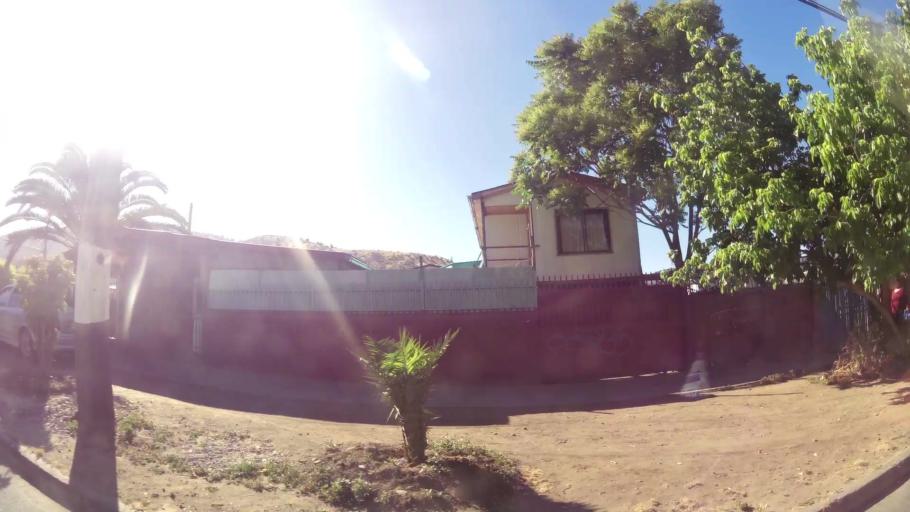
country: CL
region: Santiago Metropolitan
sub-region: Provincia de Chacabuco
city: Lampa
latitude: -33.3921
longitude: -71.1239
